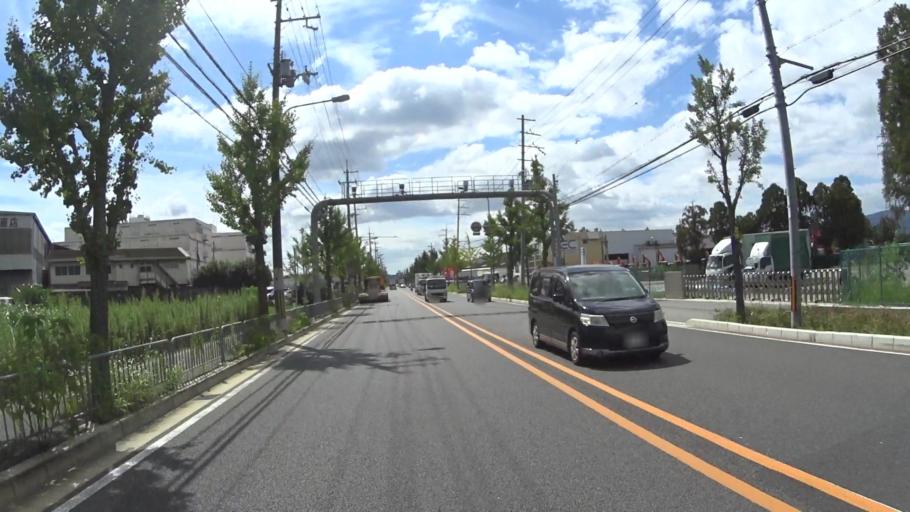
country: JP
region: Kyoto
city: Muko
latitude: 34.9195
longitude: 135.7311
